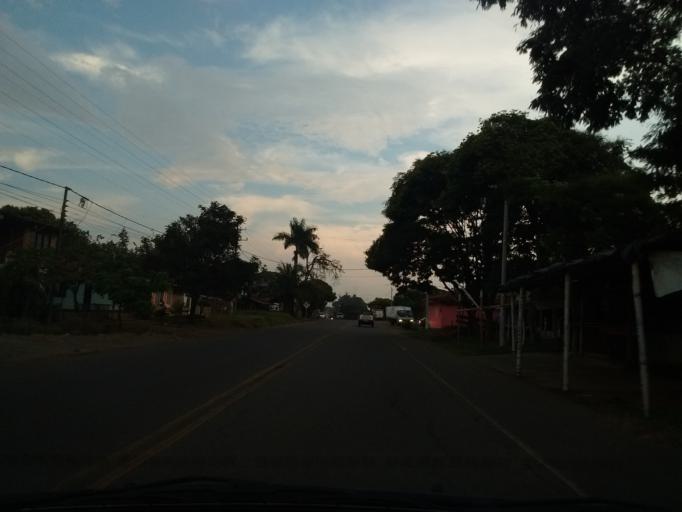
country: CO
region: Cauca
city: Santander de Quilichao
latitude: 3.0001
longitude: -76.4929
